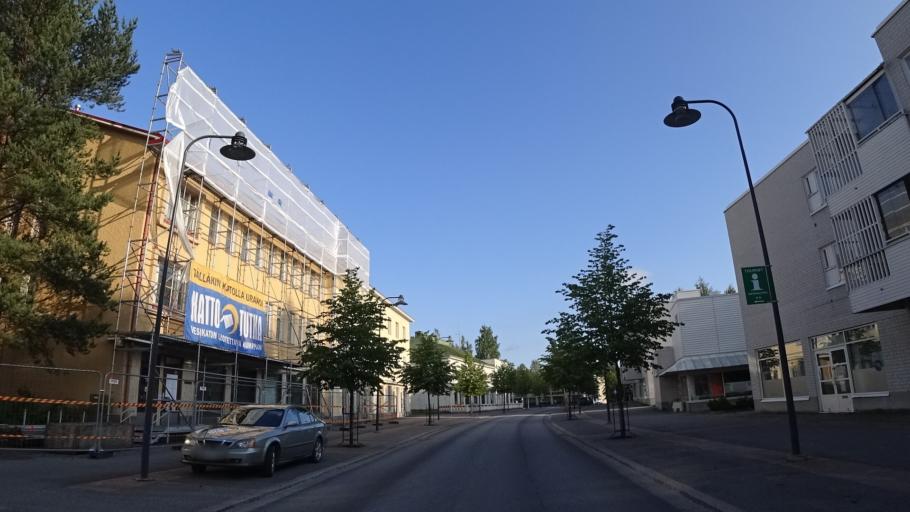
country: FI
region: North Karelia
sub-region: Pielisen Karjala
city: Lieksa
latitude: 63.3158
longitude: 30.0323
